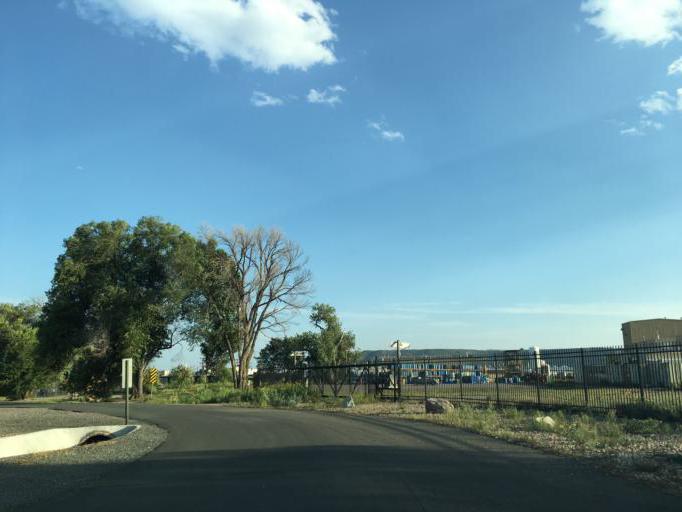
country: US
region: Colorado
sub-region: Jefferson County
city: Applewood
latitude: 39.7822
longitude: -105.1669
